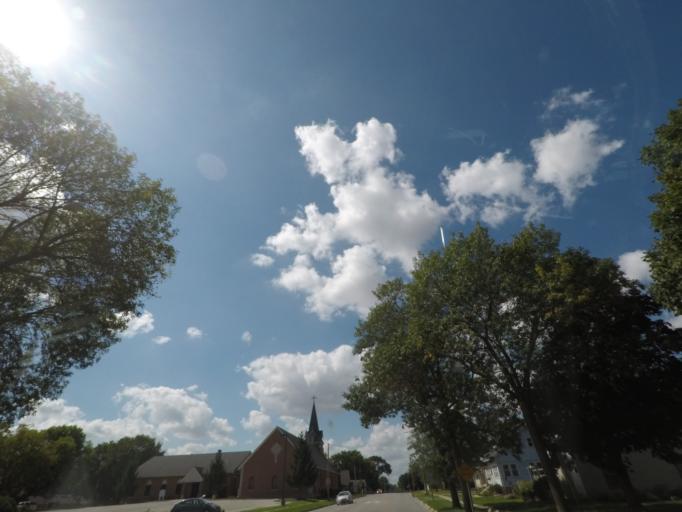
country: US
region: Iowa
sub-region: Story County
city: Nevada
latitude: 42.0228
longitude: -93.4453
